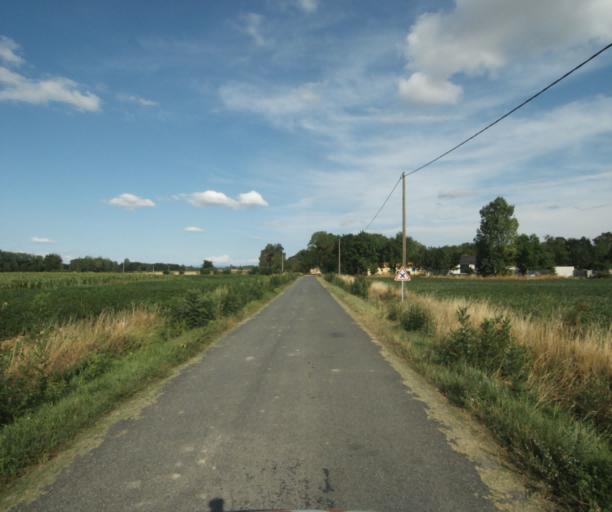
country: FR
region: Midi-Pyrenees
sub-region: Departement du Tarn
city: Puylaurens
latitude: 43.5194
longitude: 1.9989
